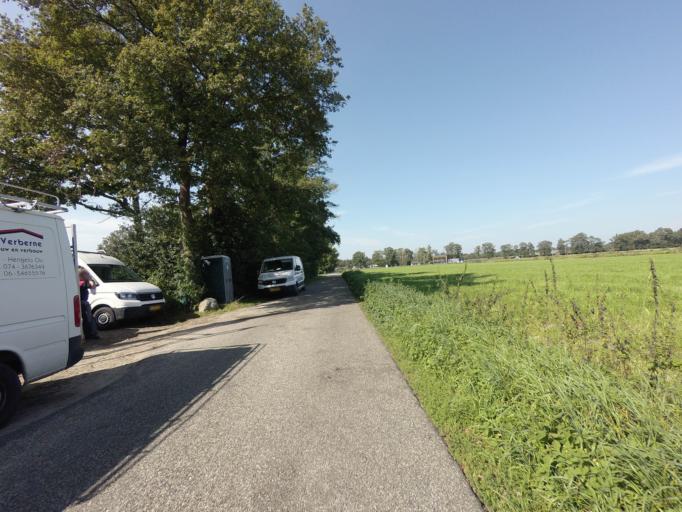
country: NL
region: Overijssel
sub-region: Gemeente Haaksbergen
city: Haaksbergen
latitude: 52.2119
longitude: 6.7566
